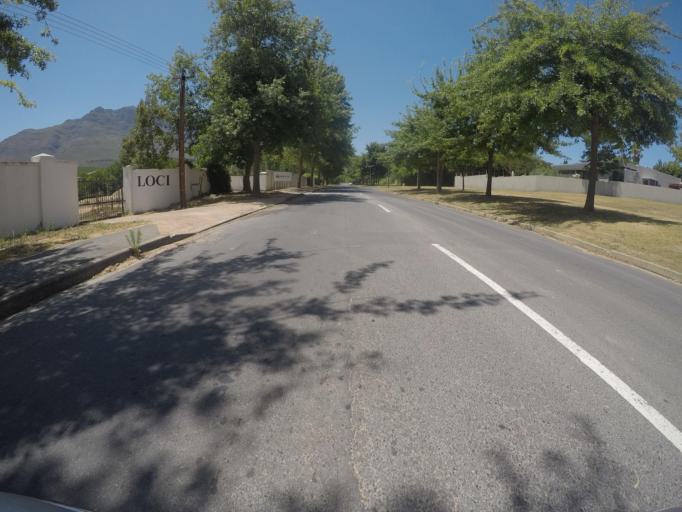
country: ZA
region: Western Cape
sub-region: Cape Winelands District Municipality
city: Stellenbosch
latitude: -33.9623
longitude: 18.8567
